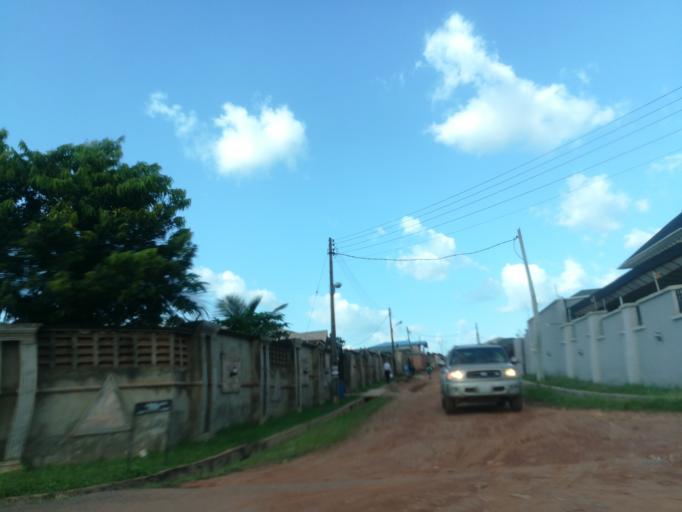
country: NG
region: Oyo
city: Ibadan
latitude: 7.4375
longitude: 3.9531
